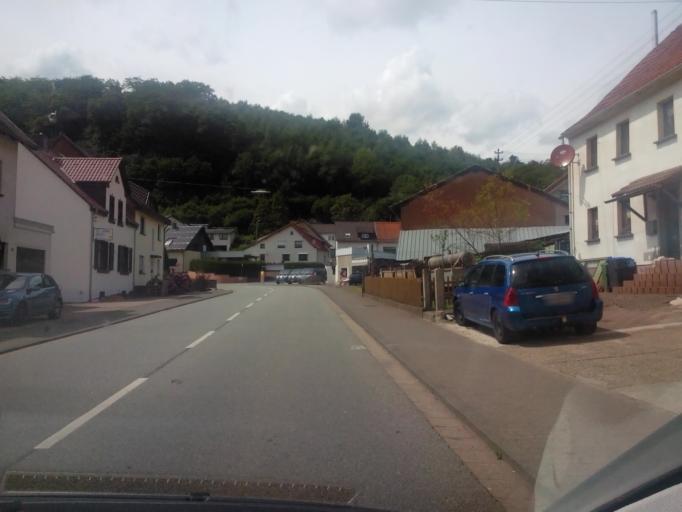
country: DE
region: Saarland
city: Eppelborn
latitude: 49.4199
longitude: 7.0038
